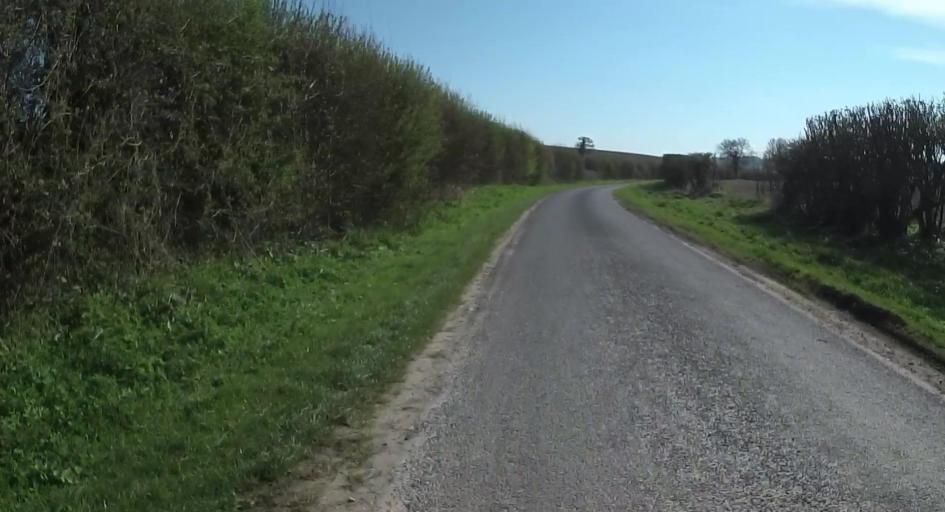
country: GB
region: England
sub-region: Hampshire
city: Highclere
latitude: 51.2666
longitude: -1.3906
